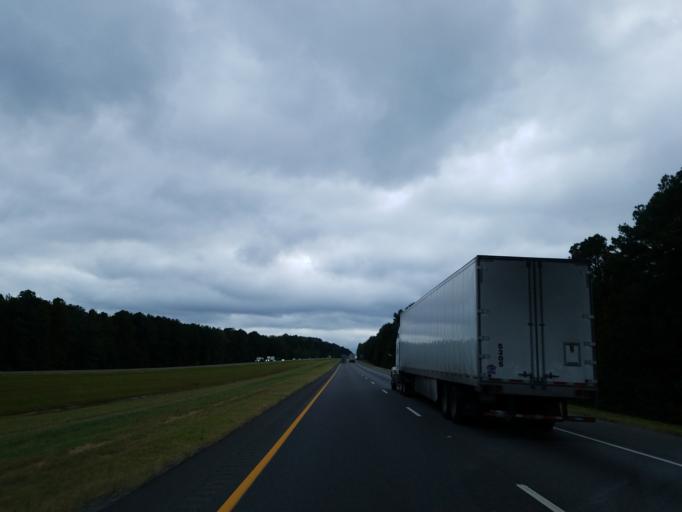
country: US
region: Alabama
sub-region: Hale County
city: Moundville
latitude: 32.9968
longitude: -87.7751
